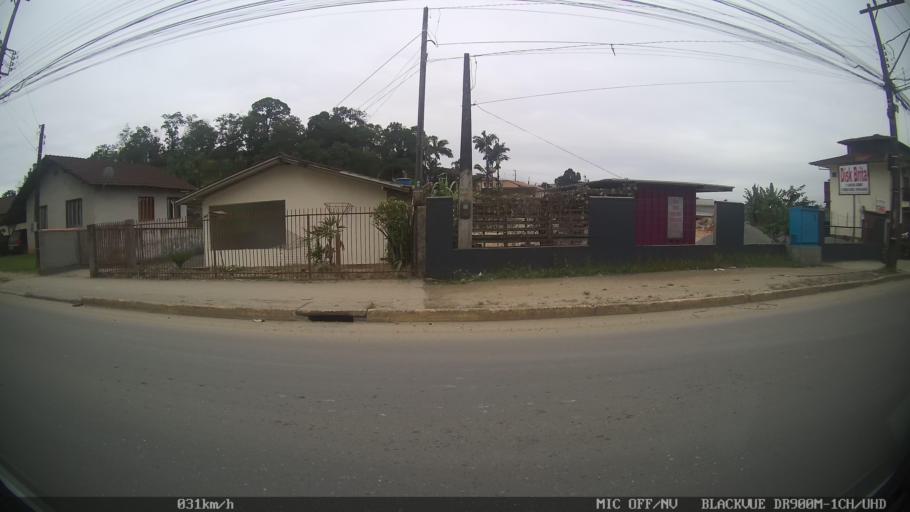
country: BR
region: Santa Catarina
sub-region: Joinville
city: Joinville
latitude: -26.3394
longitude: -48.8004
